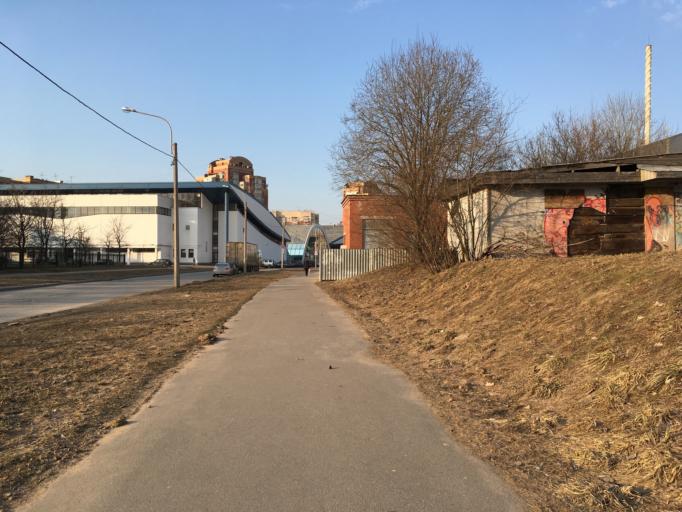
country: RU
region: St.-Petersburg
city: Komendantsky aerodrom
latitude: 60.0012
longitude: 30.2617
